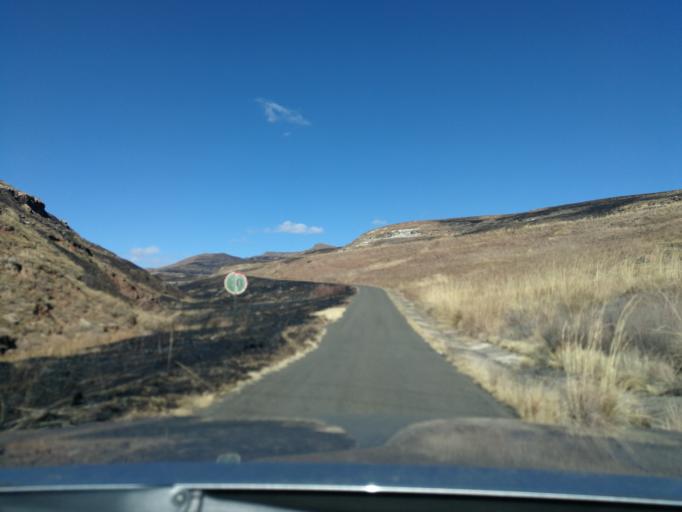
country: ZA
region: Orange Free State
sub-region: Thabo Mofutsanyana District Municipality
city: Phuthaditjhaba
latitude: -28.5100
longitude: 28.6248
